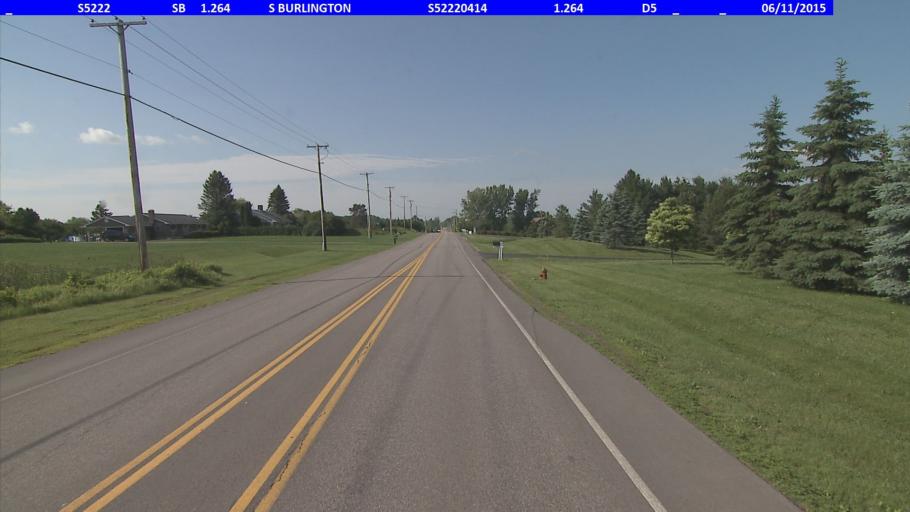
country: US
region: Vermont
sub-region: Chittenden County
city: South Burlington
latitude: 44.4348
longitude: -73.1919
